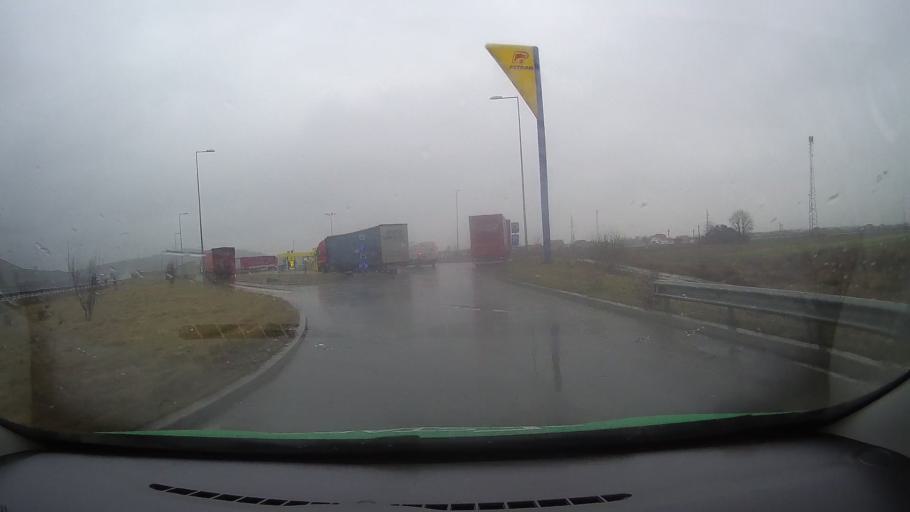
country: RO
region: Sibiu
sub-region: Comuna Cristian
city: Cristian
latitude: 45.7881
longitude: 24.0093
